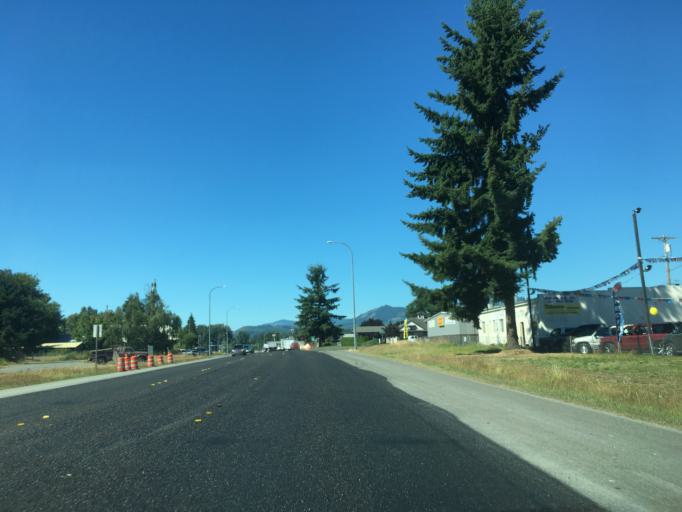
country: US
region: Washington
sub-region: Snohomish County
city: Arlington
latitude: 48.1951
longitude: -122.1288
